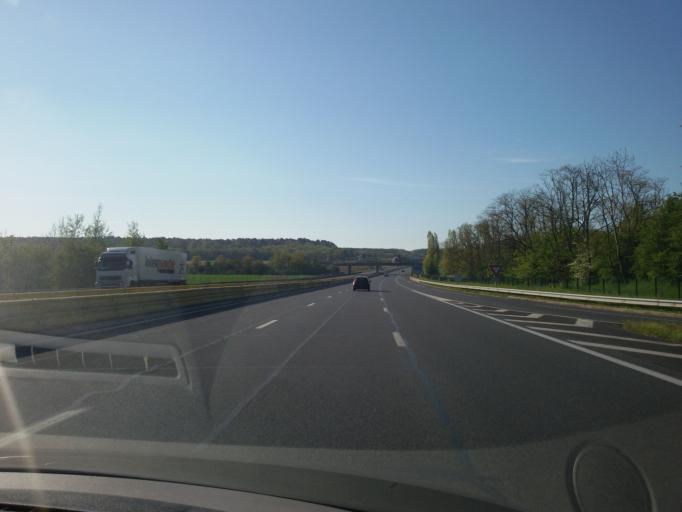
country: FR
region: Ile-de-France
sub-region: Departement de Seine-et-Marne
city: Nemours
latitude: 48.2720
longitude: 2.7141
